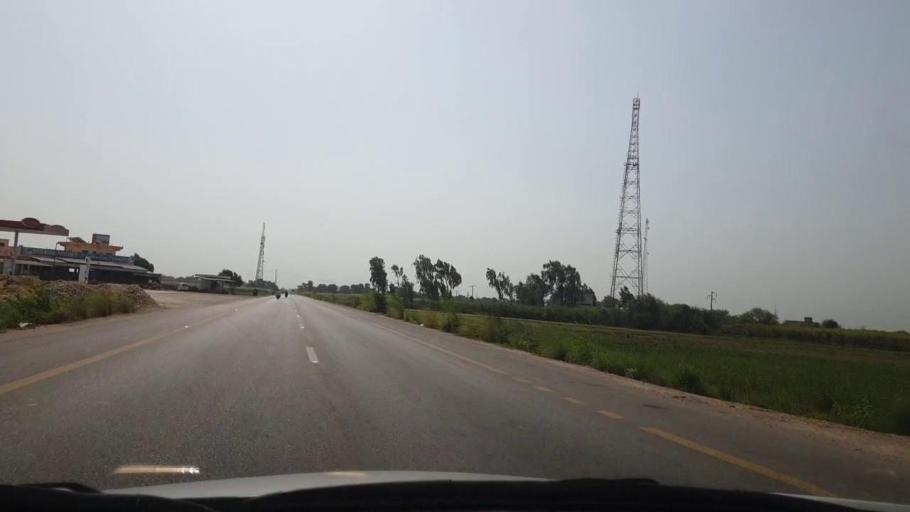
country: PK
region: Sindh
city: Tando Muhammad Khan
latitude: 25.0937
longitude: 68.5970
